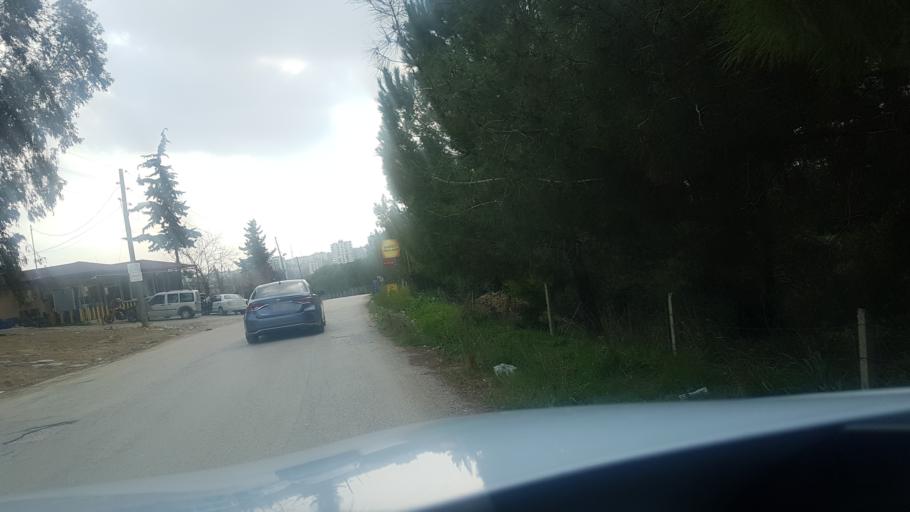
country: TR
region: Adana
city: Seyhan
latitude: 37.0592
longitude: 35.2564
